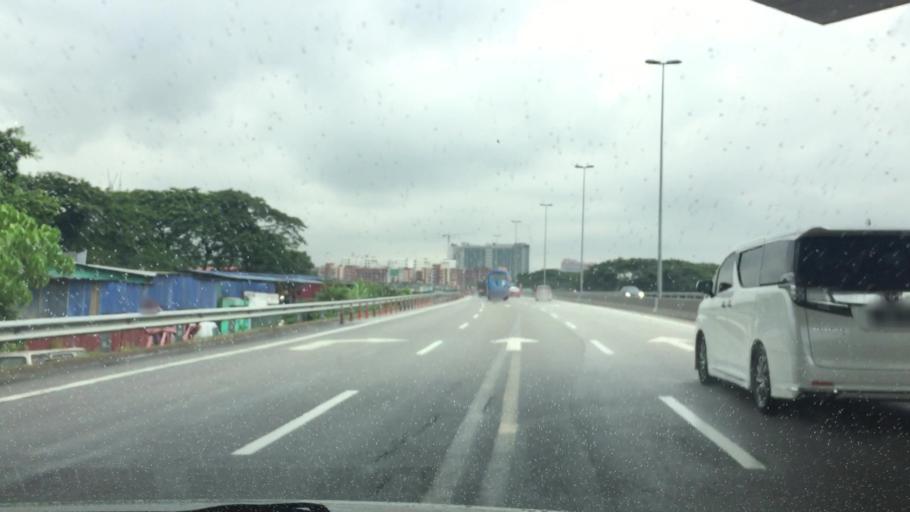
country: MY
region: Kuala Lumpur
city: Kuala Lumpur
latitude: 3.1157
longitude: 101.7133
